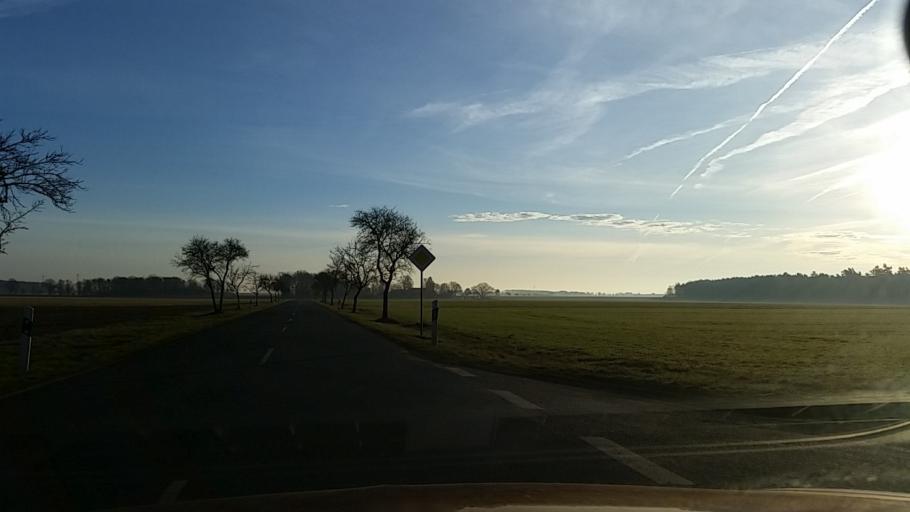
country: DE
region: Lower Saxony
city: Hankensbuttel
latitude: 52.7316
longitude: 10.5501
